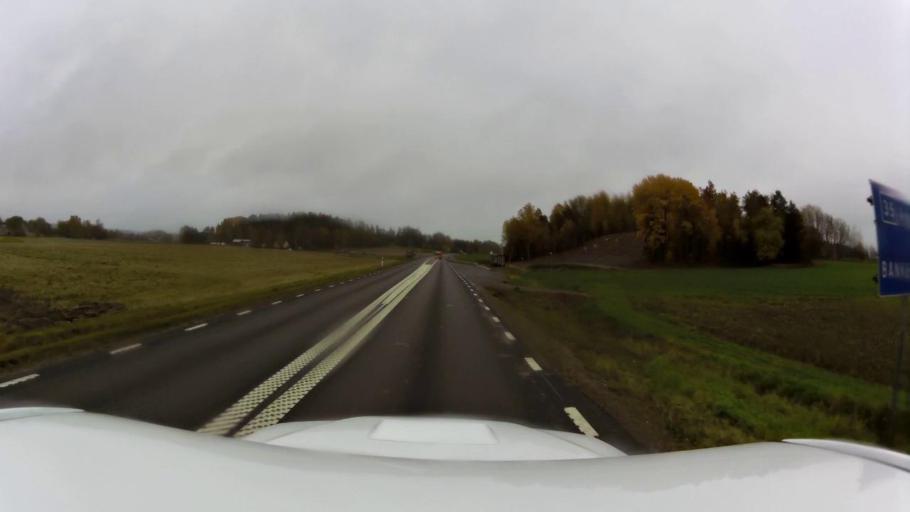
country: SE
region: OEstergoetland
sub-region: Linkopings Kommun
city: Linghem
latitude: 58.3732
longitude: 15.8121
